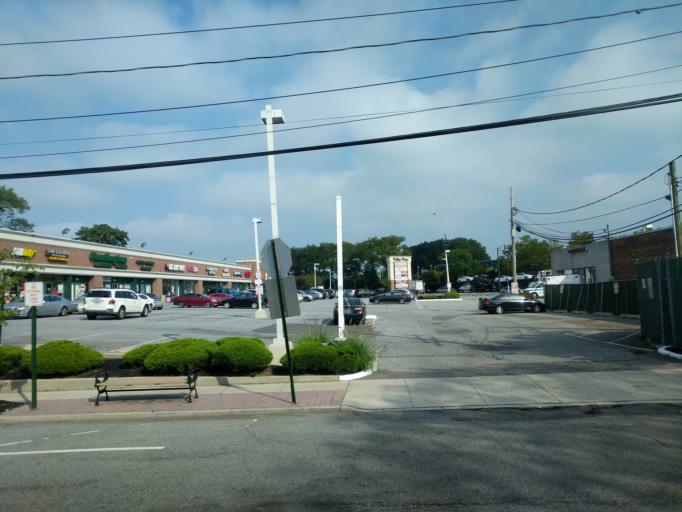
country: US
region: New York
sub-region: Nassau County
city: Lynbrook
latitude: 40.6547
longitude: -73.6751
